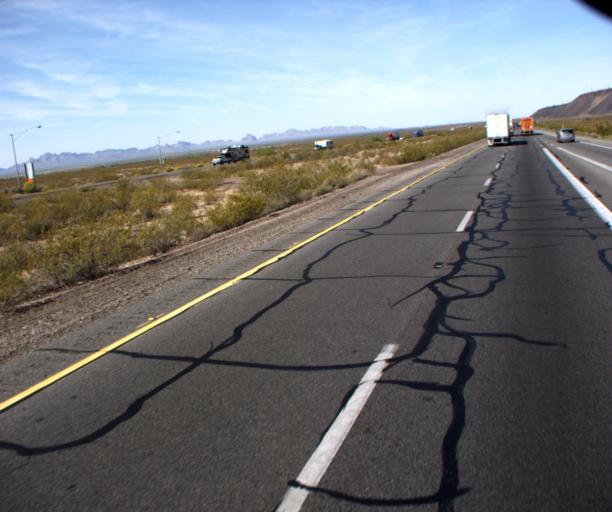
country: US
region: Arizona
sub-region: Maricopa County
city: Buckeye
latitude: 33.5214
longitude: -113.0729
